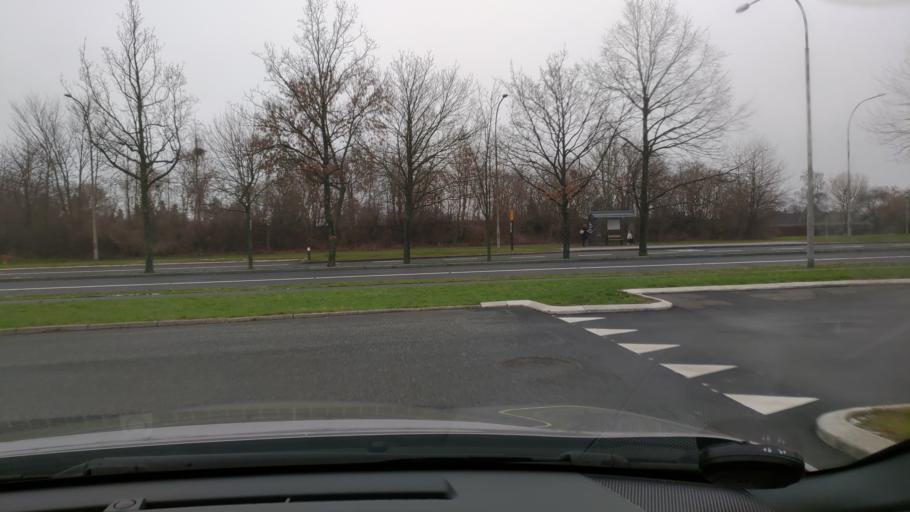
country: DK
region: Zealand
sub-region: Solrod Kommune
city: Solrod Strand
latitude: 55.5347
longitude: 12.2138
